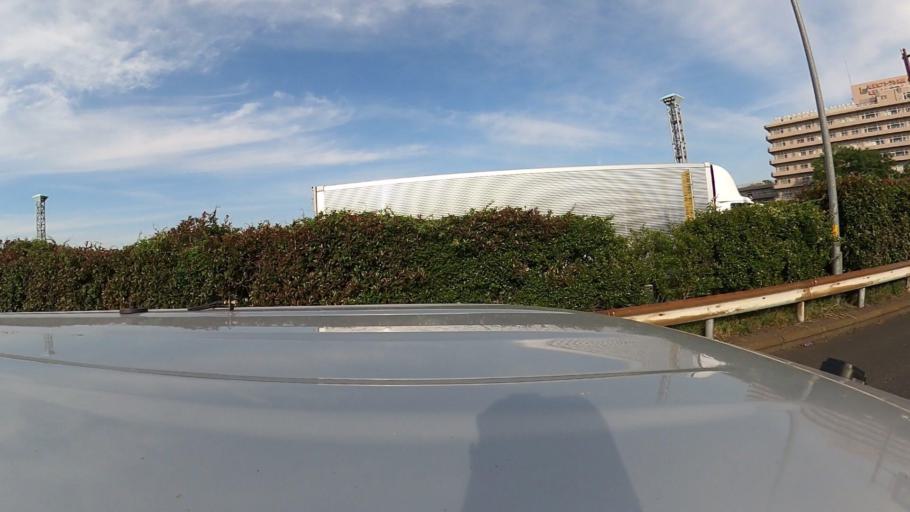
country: JP
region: Saitama
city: Oi
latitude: 35.8426
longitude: 139.5033
